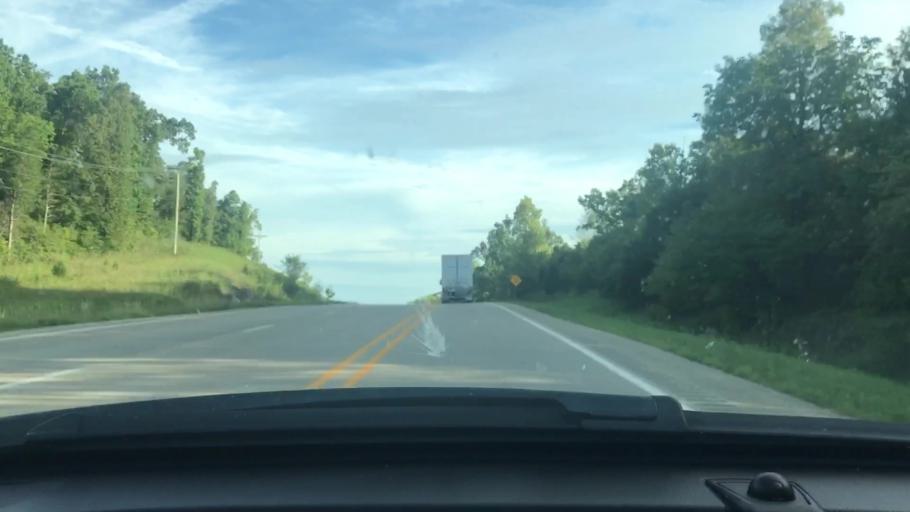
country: US
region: Arkansas
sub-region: Lawrence County
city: Hoxie
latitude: 36.1494
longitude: -91.1603
